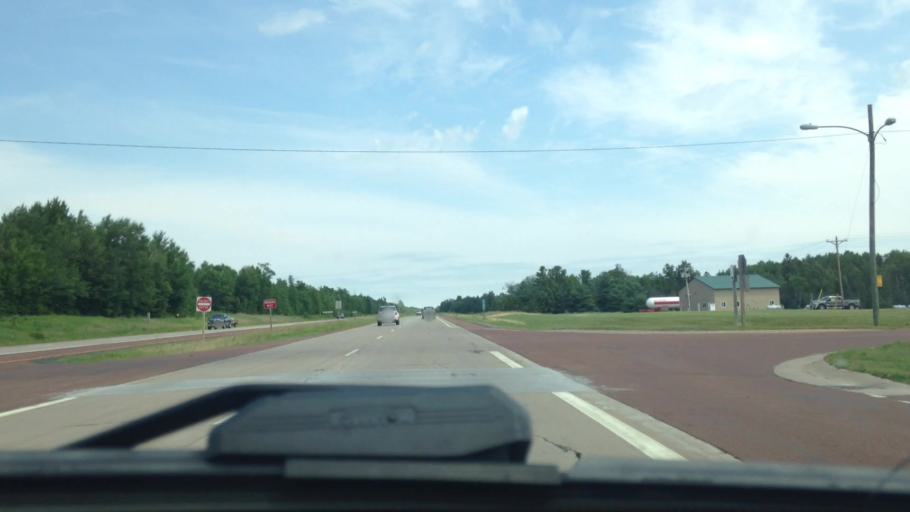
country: US
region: Wisconsin
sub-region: Douglas County
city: Lake Nebagamon
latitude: 46.3598
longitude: -91.8324
